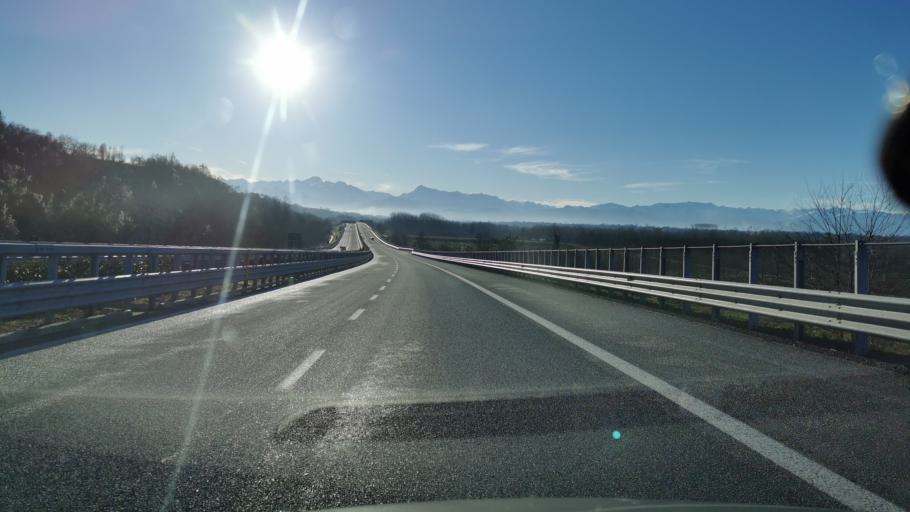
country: IT
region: Piedmont
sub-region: Provincia di Cuneo
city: Montanera
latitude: 44.4746
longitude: 7.6768
